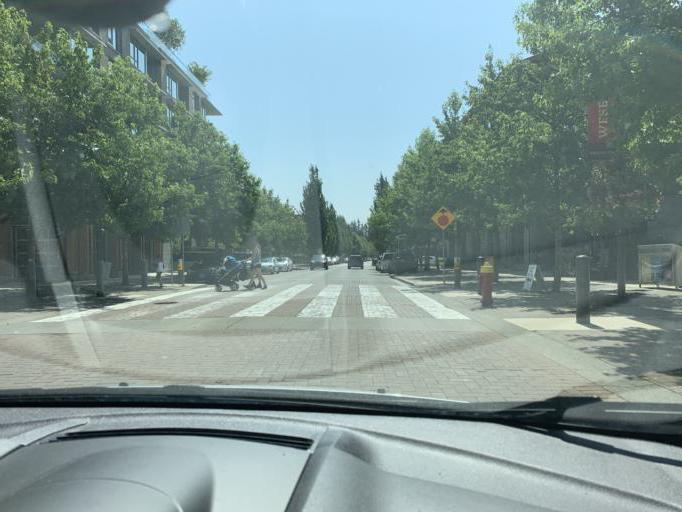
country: CA
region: British Columbia
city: West End
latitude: 49.2544
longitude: -123.2352
